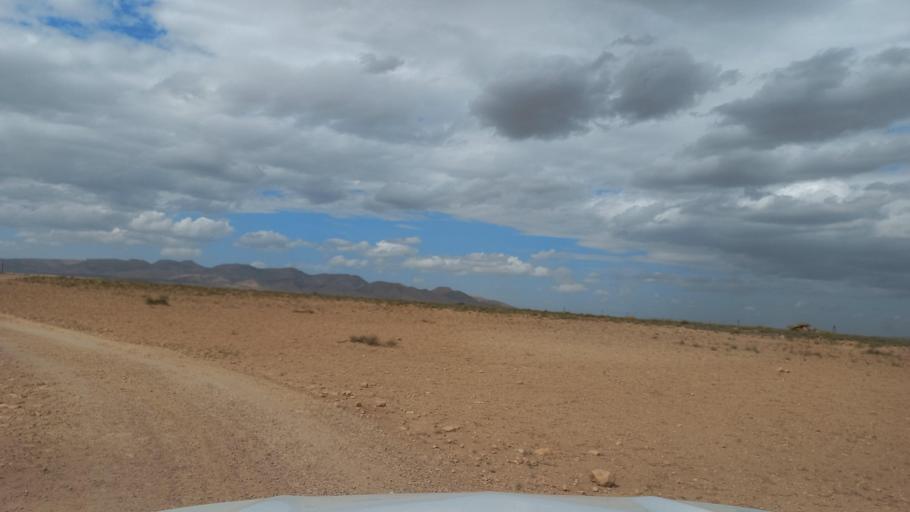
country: TN
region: Al Qasrayn
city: Sbiba
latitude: 35.3804
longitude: 9.1034
